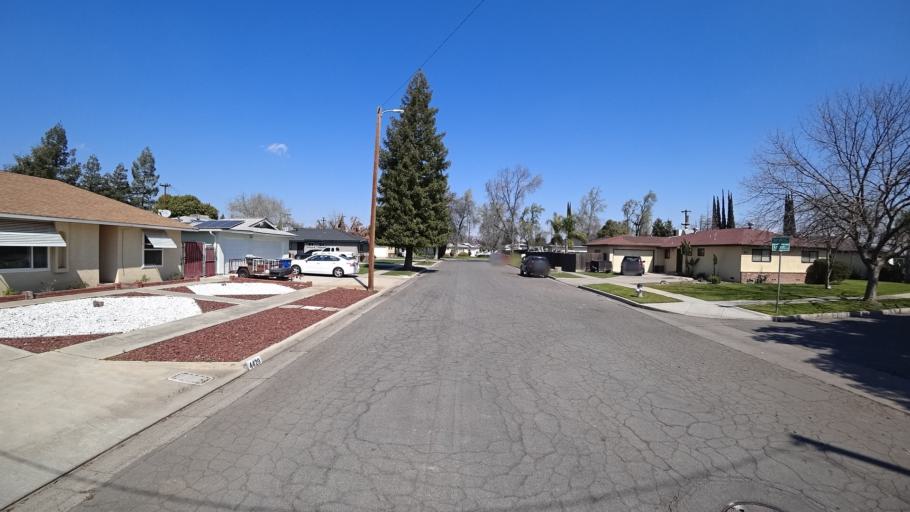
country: US
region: California
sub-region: Fresno County
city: Tarpey Village
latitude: 36.7985
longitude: -119.7405
